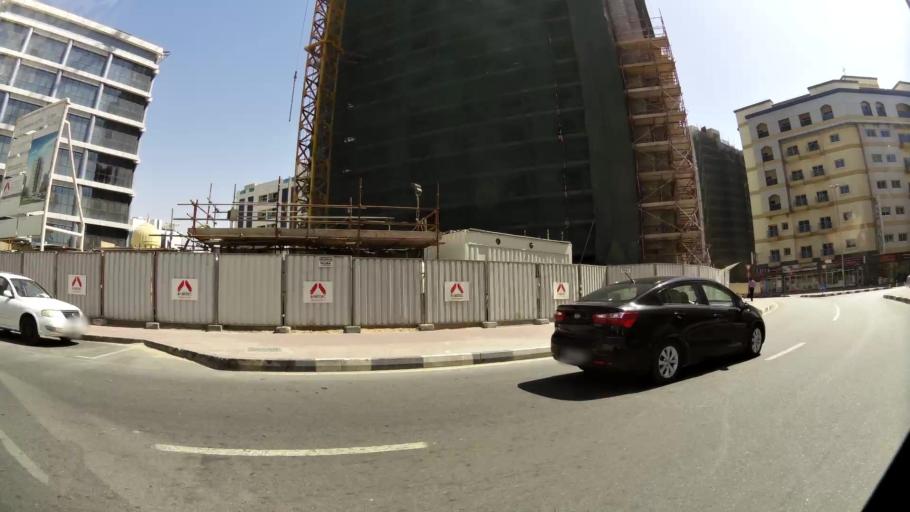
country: AE
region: Dubai
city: Dubai
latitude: 25.1141
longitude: 55.1935
